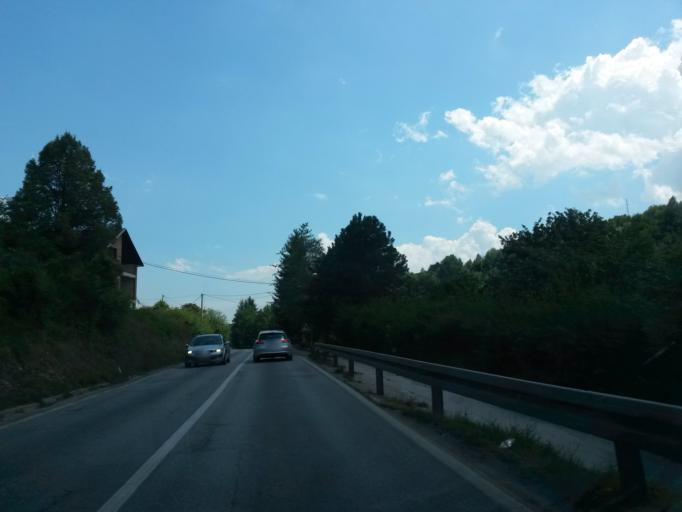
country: BA
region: Federation of Bosnia and Herzegovina
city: Turbe
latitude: 44.2340
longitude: 17.6125
